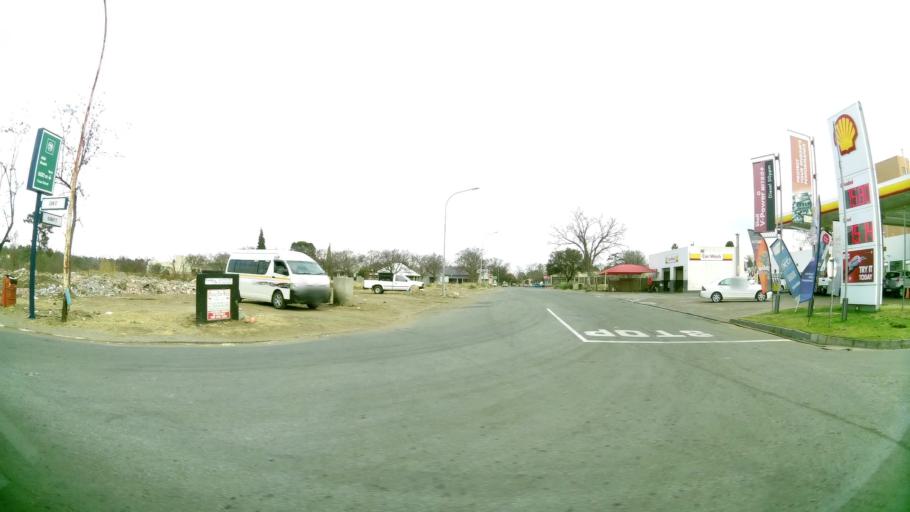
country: ZA
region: Orange Free State
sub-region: Fezile Dabi District Municipality
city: Kroonstad
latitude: -27.6707
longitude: 27.2361
